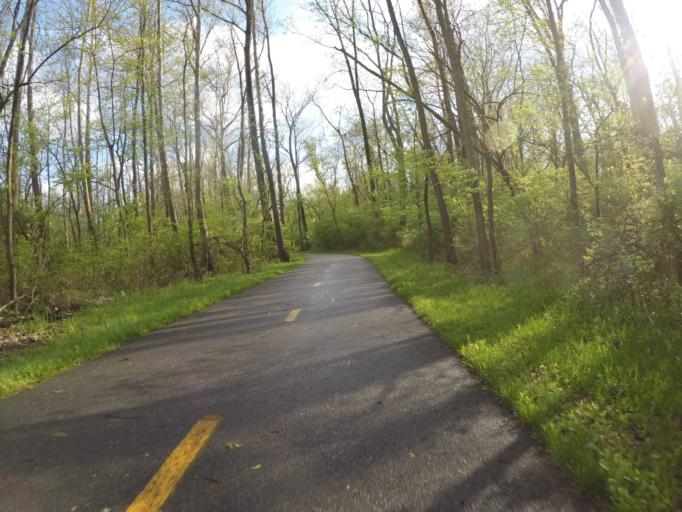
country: US
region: Ohio
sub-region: Franklin County
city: Bexley
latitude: 40.0001
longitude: -82.9368
